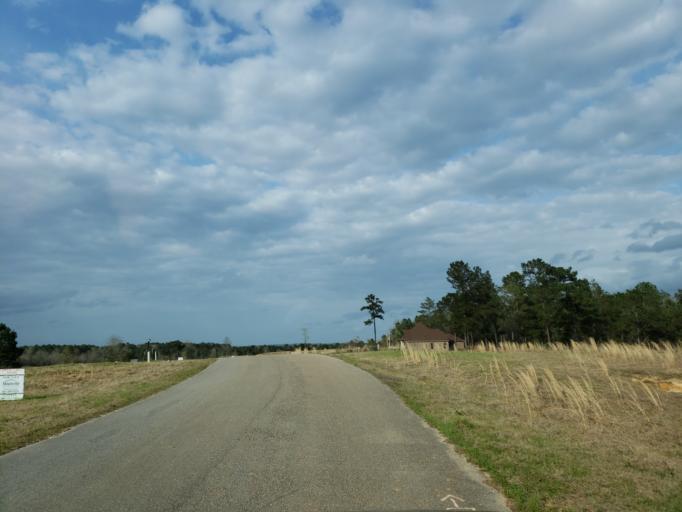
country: US
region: Mississippi
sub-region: Jones County
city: Ellisville
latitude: 31.5592
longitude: -89.2531
